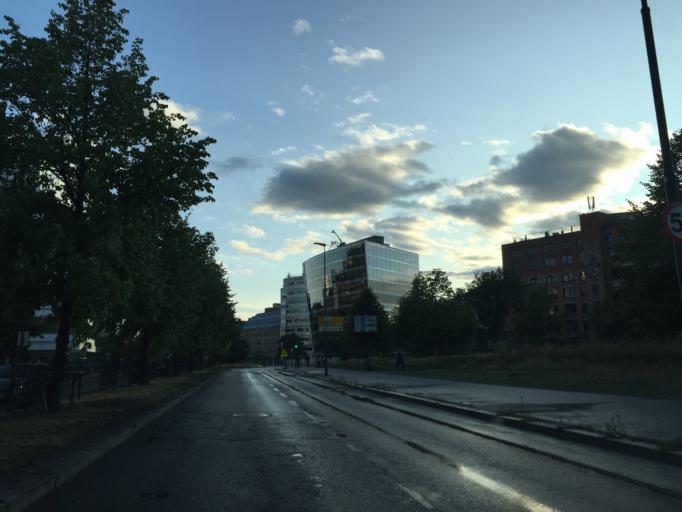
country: NO
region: Oslo
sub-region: Oslo
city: Oslo
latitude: 59.9159
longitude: 10.7622
